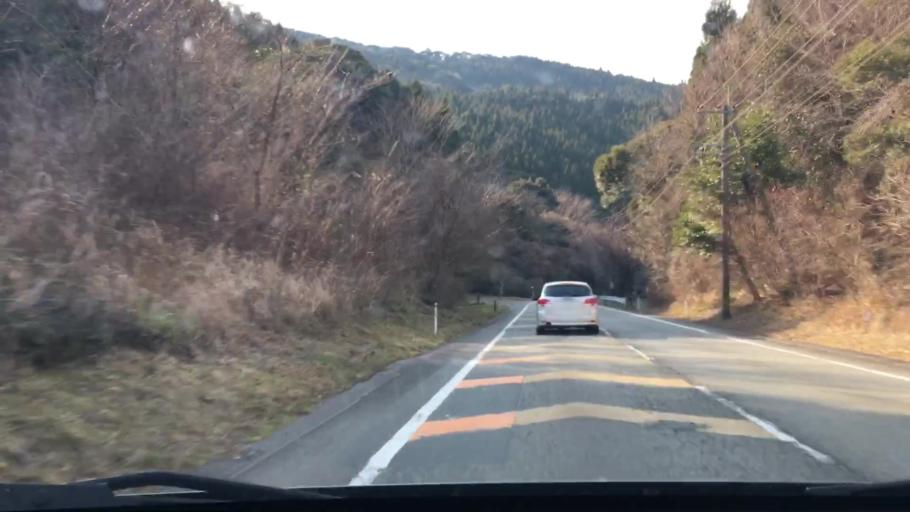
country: JP
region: Miyazaki
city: Miyazaki-shi
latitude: 31.7903
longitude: 131.3183
